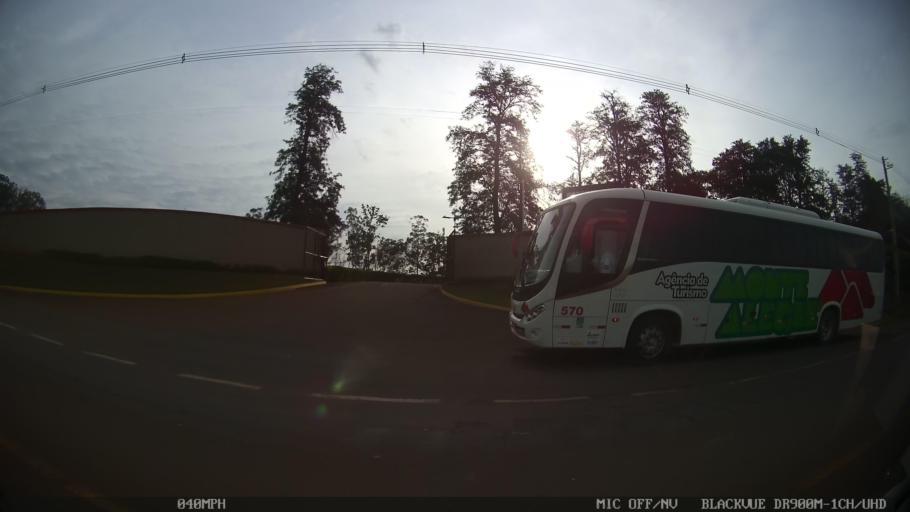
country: BR
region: Sao Paulo
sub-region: Piracicaba
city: Piracicaba
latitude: -22.7181
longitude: -47.5826
